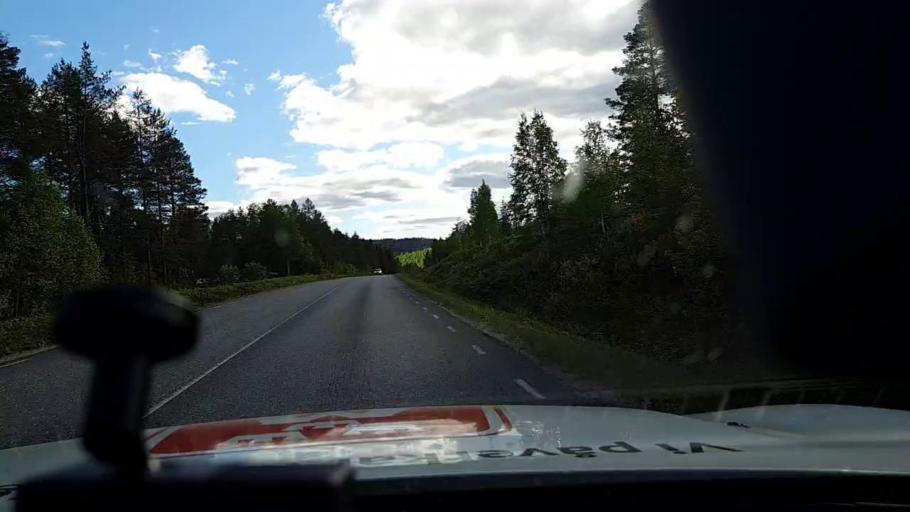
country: FI
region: Lapland
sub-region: Torniolaakso
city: Ylitornio
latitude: 66.3327
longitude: 23.6382
